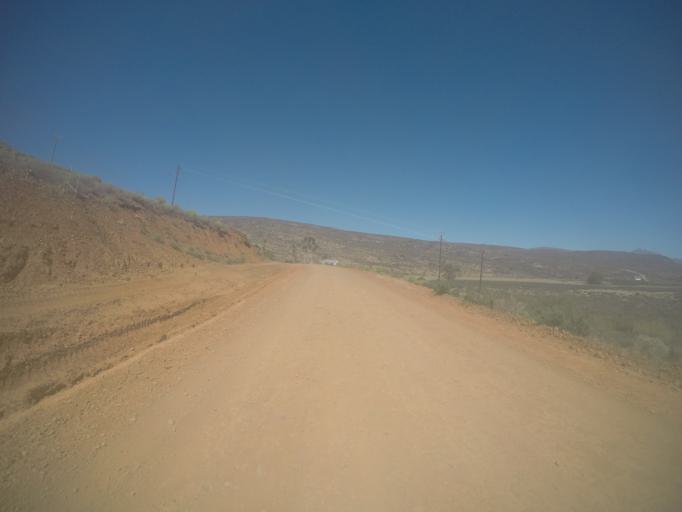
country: ZA
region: Western Cape
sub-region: West Coast District Municipality
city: Clanwilliam
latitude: -32.5007
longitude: 19.3385
